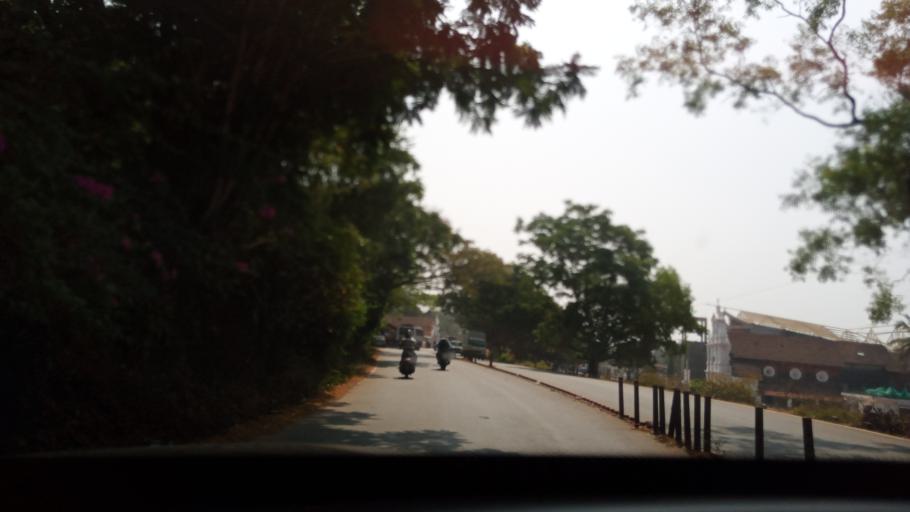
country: IN
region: Goa
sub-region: South Goa
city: Raia
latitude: 15.3091
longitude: 73.9459
